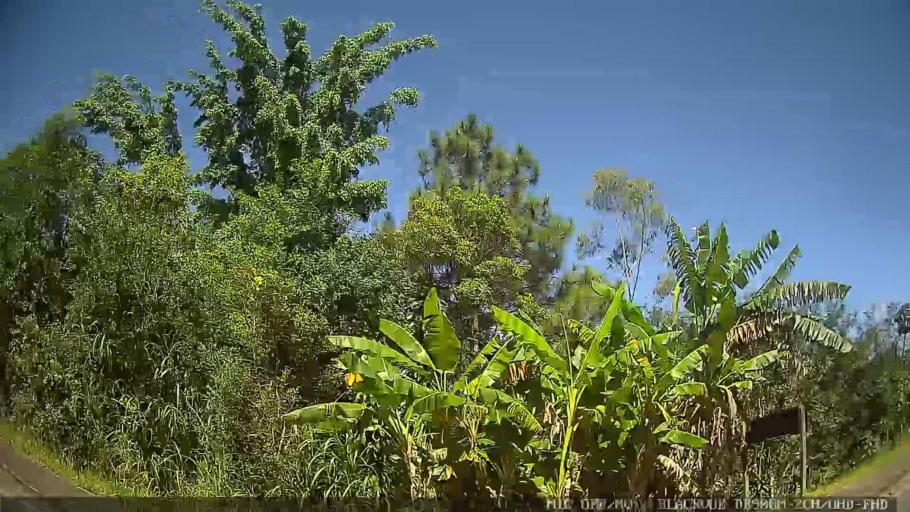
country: BR
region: Sao Paulo
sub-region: Suzano
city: Suzano
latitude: -23.6083
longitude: -46.2552
